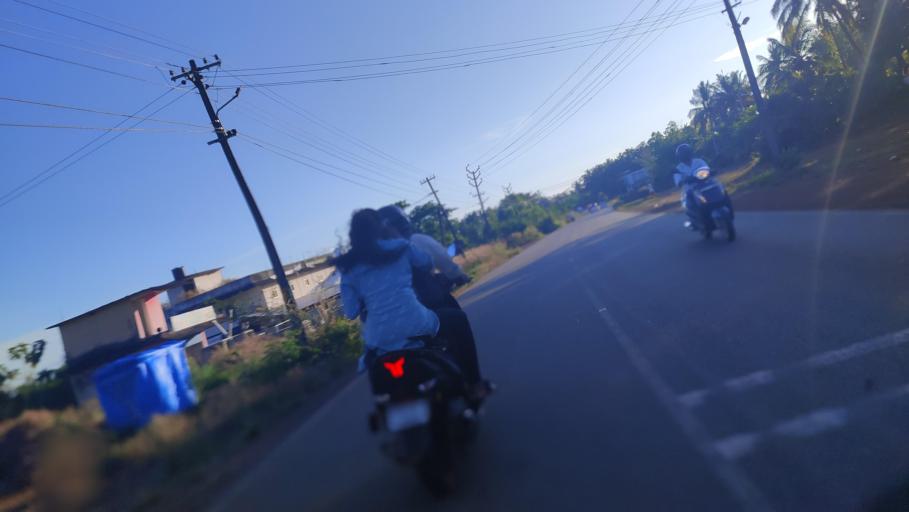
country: IN
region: Kerala
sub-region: Kasaragod District
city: Kasaragod
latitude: 12.4735
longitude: 75.0595
